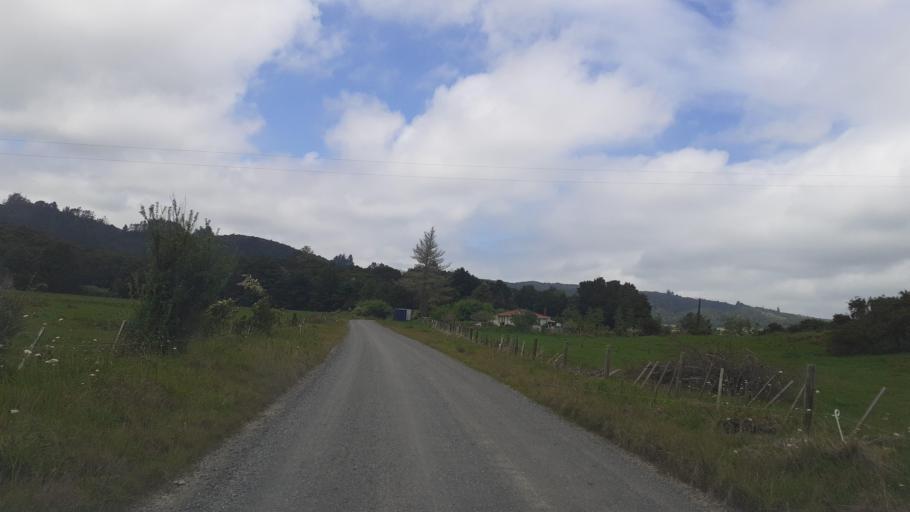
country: NZ
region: Northland
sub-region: Far North District
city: Kawakawa
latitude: -35.4168
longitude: 174.0839
